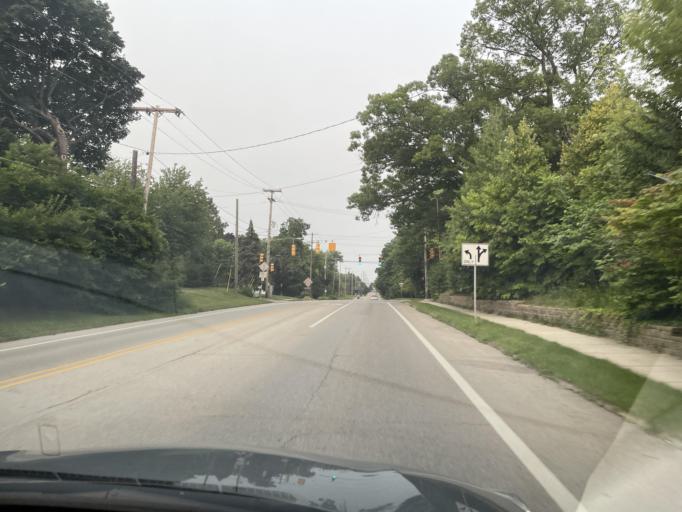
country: US
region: Michigan
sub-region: Kent County
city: East Grand Rapids
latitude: 42.9627
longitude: -85.6232
